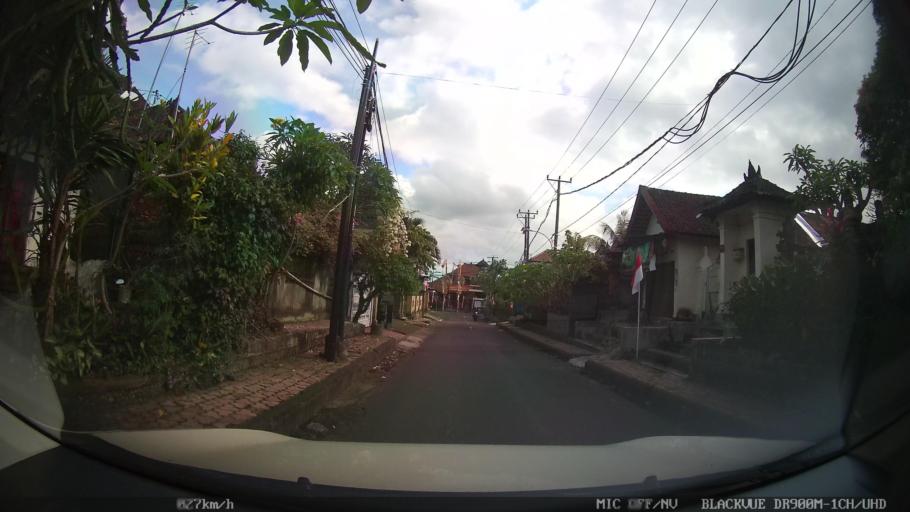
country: ID
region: Bali
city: Banjar Tegal Belodan
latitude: -8.5401
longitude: 115.1216
